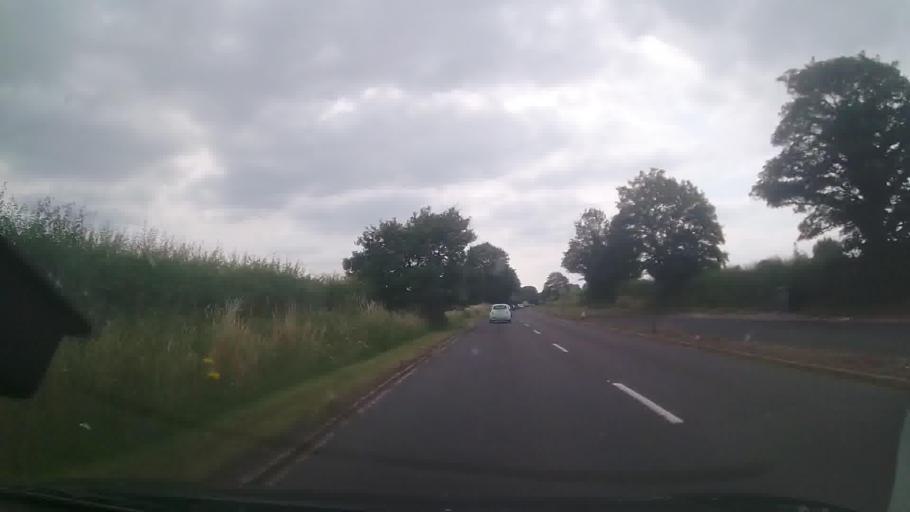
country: GB
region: England
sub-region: Shropshire
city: Market Drayton
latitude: 52.9115
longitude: -2.4512
